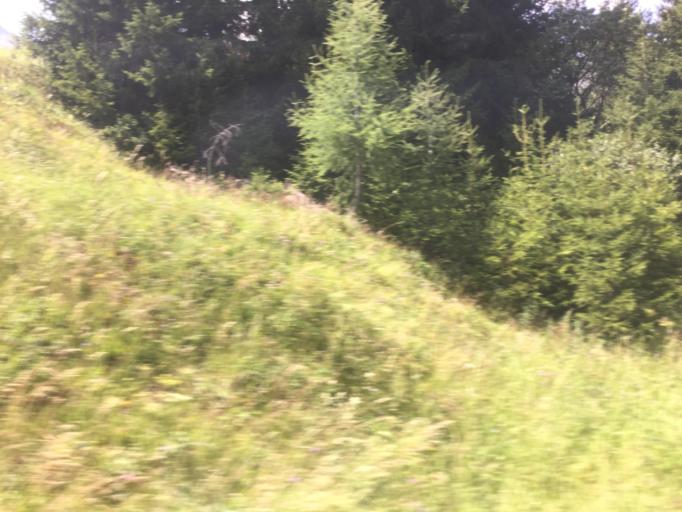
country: CH
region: Grisons
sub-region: Maloja District
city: Silvaplana
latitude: 46.4838
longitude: 9.6414
